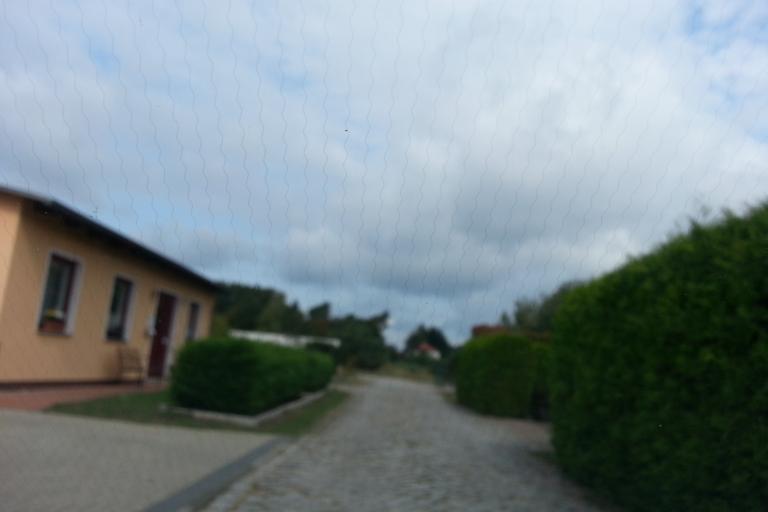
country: DE
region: Mecklenburg-Vorpommern
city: Torgelow
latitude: 53.6278
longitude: 13.9961
